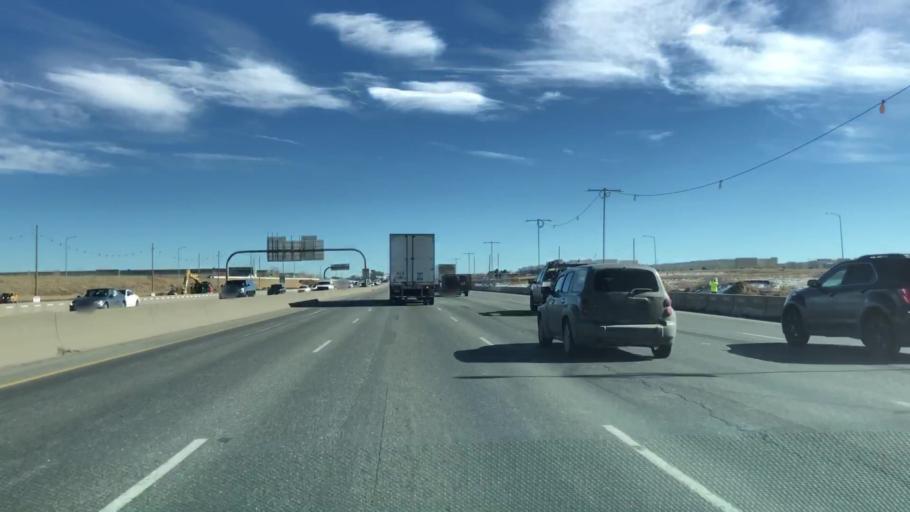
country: US
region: Colorado
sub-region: Adams County
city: Commerce City
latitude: 39.7754
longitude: -104.8814
